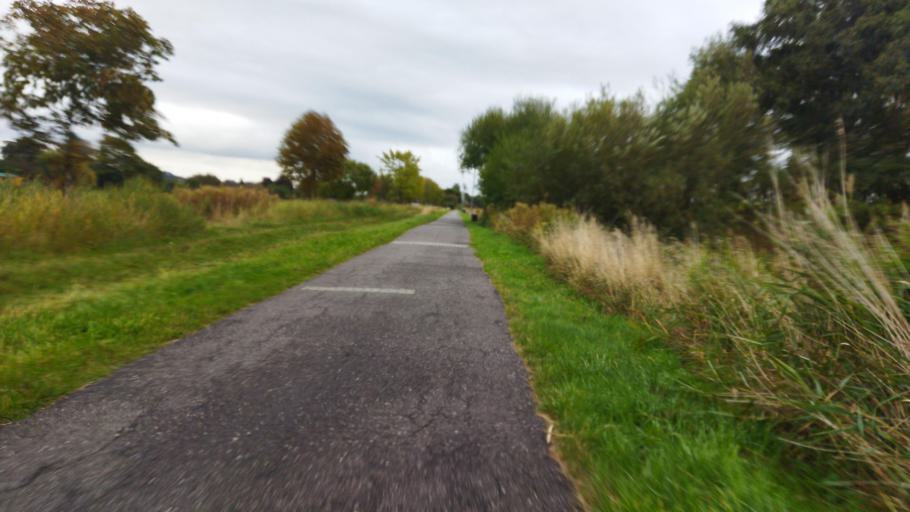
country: DE
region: Lower Saxony
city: Hinte
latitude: 53.4036
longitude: 7.1957
